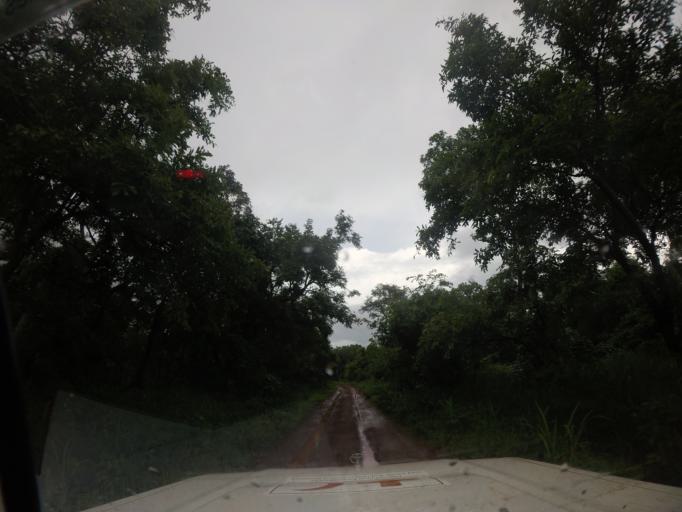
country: SL
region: Northern Province
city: Kamakwie
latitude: 9.7946
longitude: -12.3594
